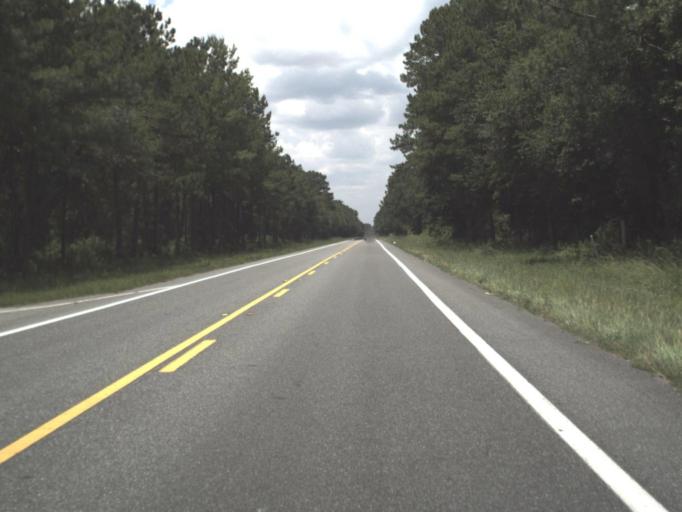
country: US
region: Florida
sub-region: Columbia County
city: Five Points
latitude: 30.2294
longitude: -82.6635
